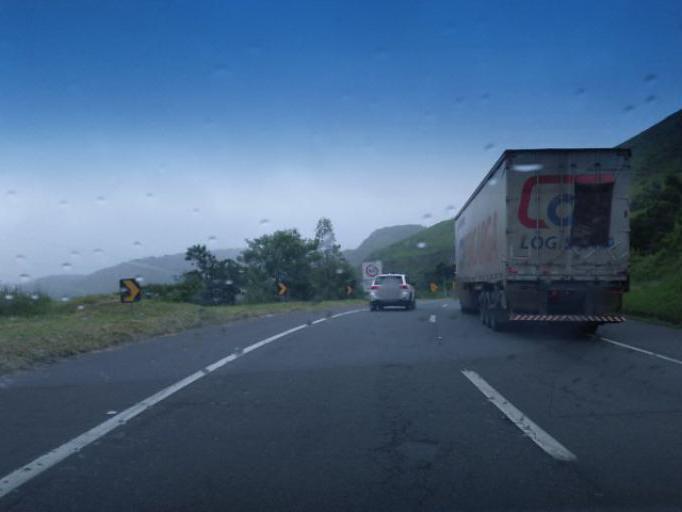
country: BR
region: Sao Paulo
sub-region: Cajati
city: Cajati
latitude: -24.9663
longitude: -48.4754
